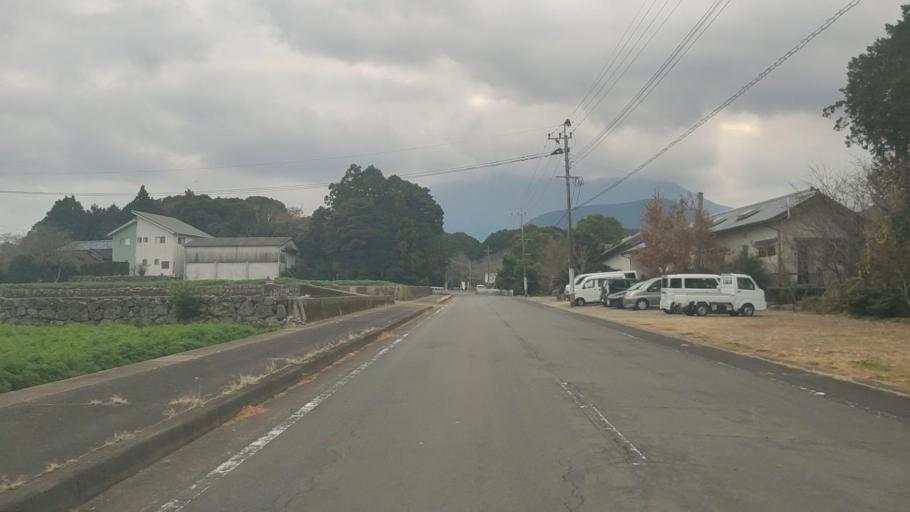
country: JP
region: Nagasaki
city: Shimabara
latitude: 32.8206
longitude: 130.2911
